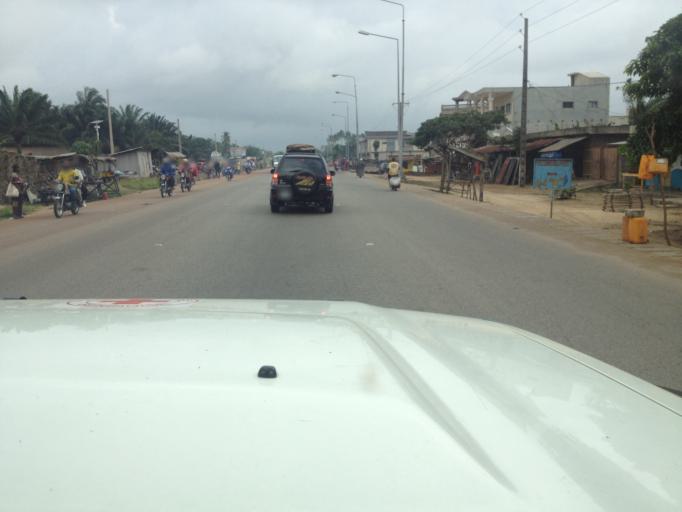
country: BJ
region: Queme
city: Porto-Novo
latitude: 6.4347
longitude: 2.6247
